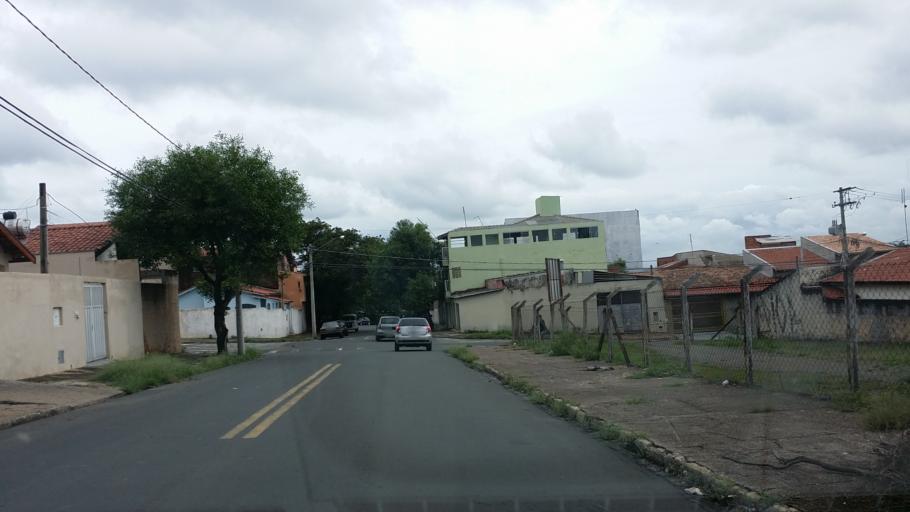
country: BR
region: Sao Paulo
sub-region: Indaiatuba
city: Indaiatuba
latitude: -23.1255
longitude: -47.2291
